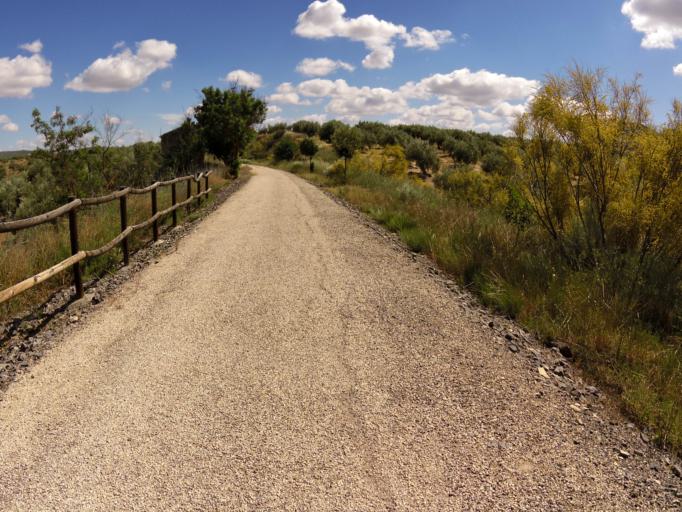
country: ES
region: Andalusia
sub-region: Provincia de Jaen
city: Alcaudete
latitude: 37.6315
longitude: -4.0840
